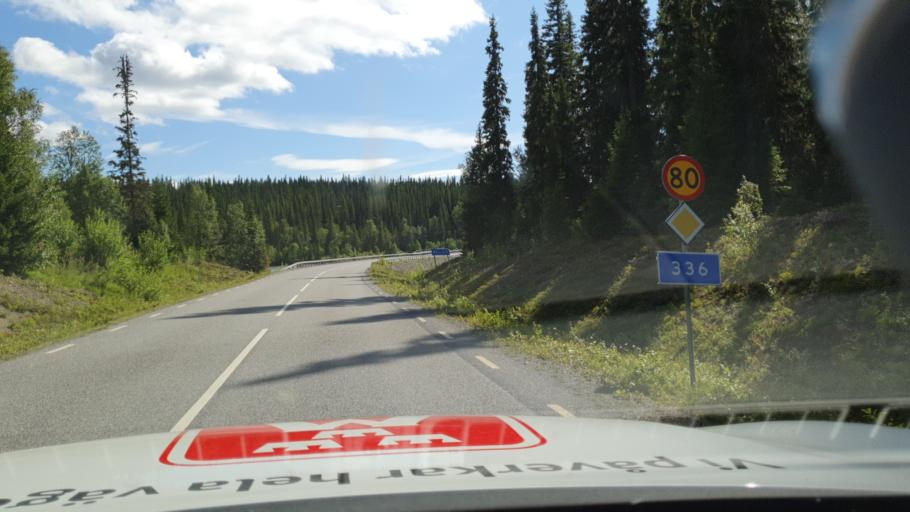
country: SE
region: Jaemtland
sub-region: Are Kommun
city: Are
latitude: 63.6750
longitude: 13.0524
